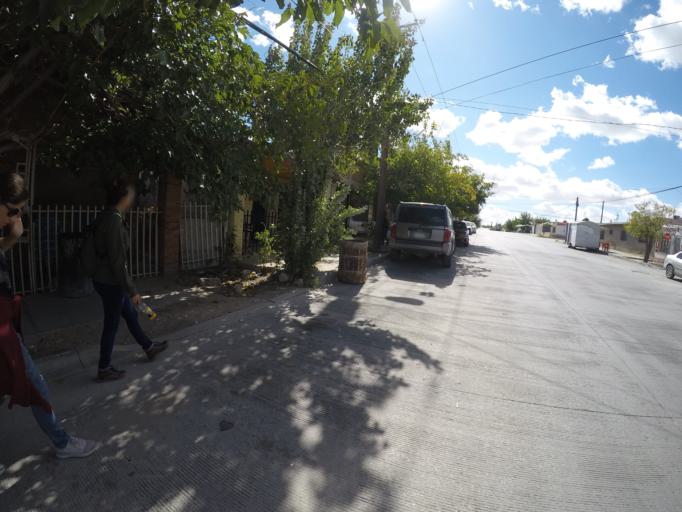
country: MX
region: Chihuahua
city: Ciudad Juarez
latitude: 31.6906
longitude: -106.4816
